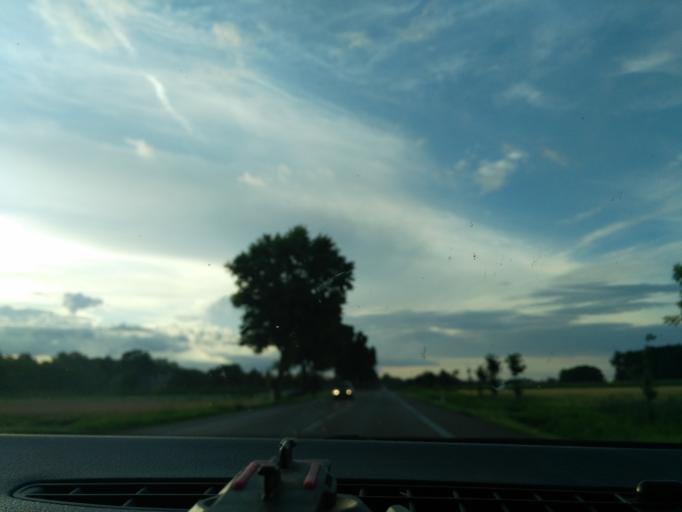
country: PL
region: Lublin Voivodeship
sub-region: Powiat lubelski
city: Niedrzwica Duza
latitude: 51.0817
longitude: 22.3722
